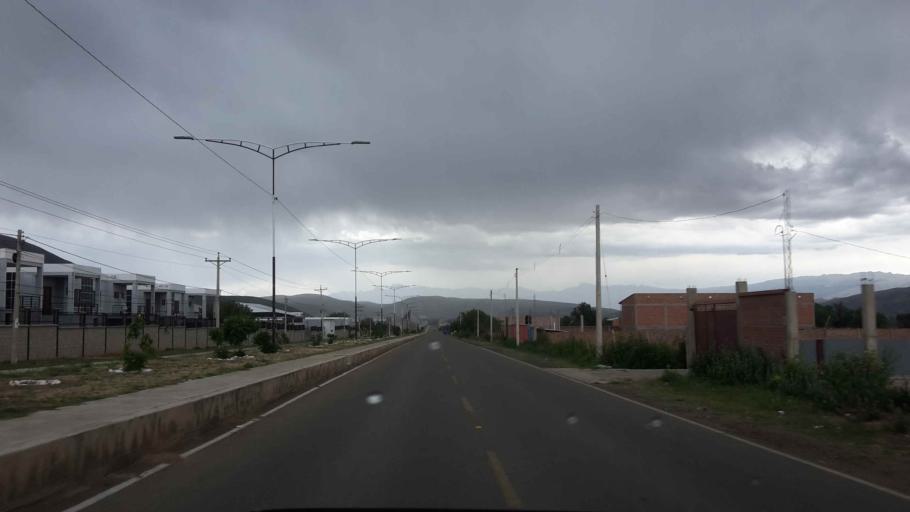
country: BO
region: Cochabamba
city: Tarata
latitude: -17.6014
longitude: -66.0345
